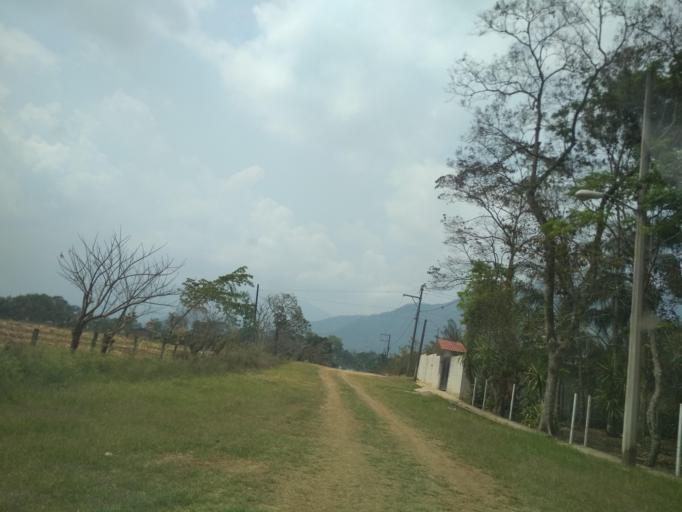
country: MX
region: Veracruz
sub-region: Cordoba
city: San Jose de Tapia
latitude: 18.8509
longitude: -96.9783
